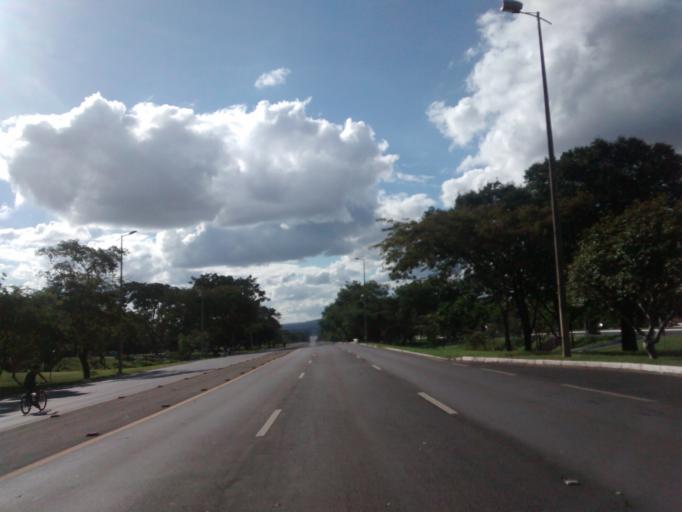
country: BR
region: Federal District
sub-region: Brasilia
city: Brasilia
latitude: -15.7655
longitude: -47.8830
